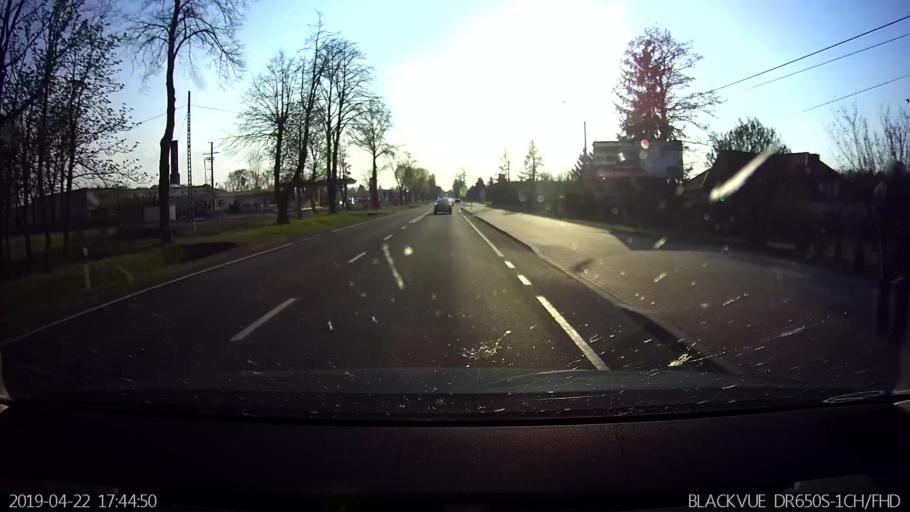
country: PL
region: Masovian Voivodeship
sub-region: Powiat wegrowski
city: Wegrow
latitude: 52.4016
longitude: 22.0442
